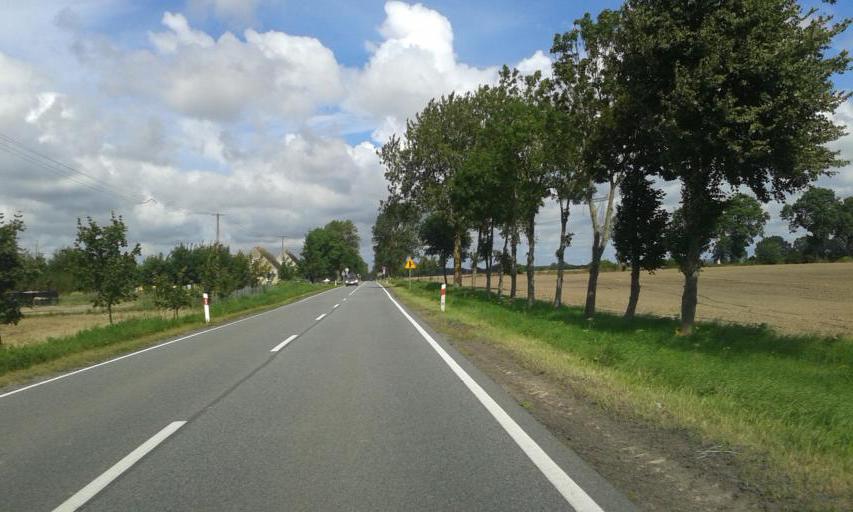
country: PL
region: West Pomeranian Voivodeship
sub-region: Powiat slawienski
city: Slawno
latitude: 54.3313
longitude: 16.5521
